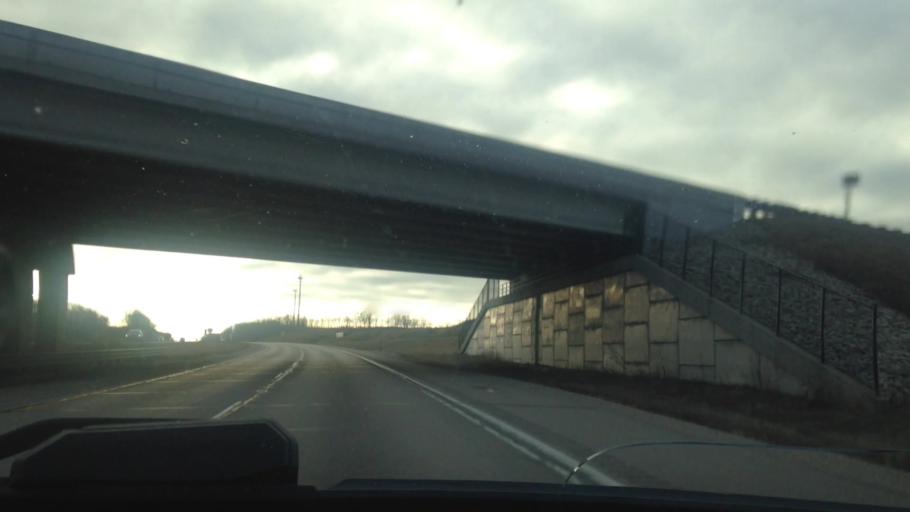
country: US
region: Wisconsin
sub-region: Washington County
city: Slinger
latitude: 43.3476
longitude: -88.2827
